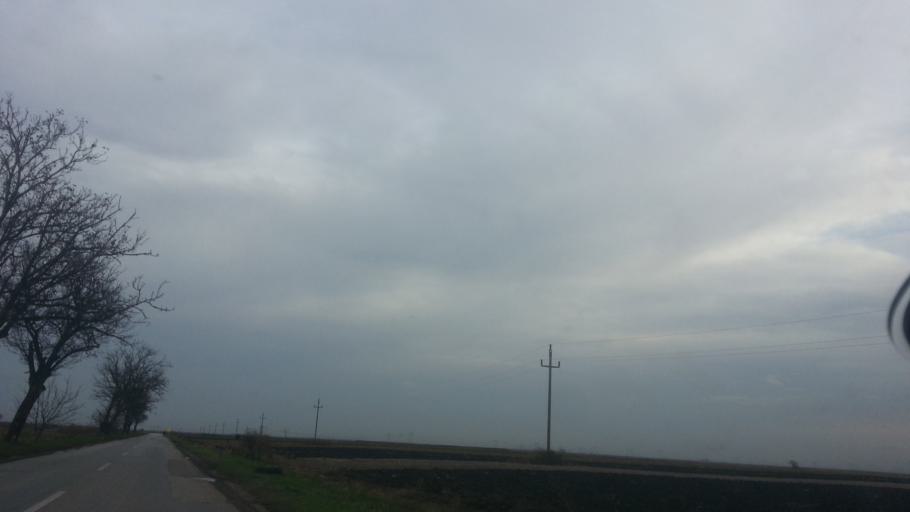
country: RS
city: Golubinci
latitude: 44.9801
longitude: 20.0879
